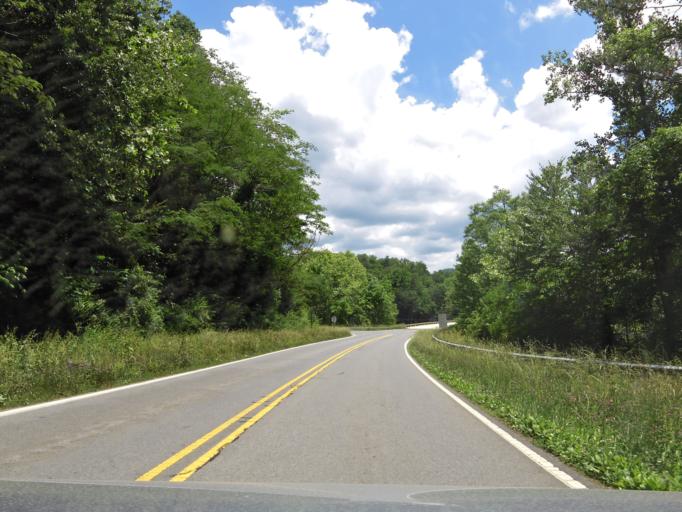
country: US
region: North Carolina
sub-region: Graham County
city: Robbinsville
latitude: 35.3452
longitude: -83.8162
